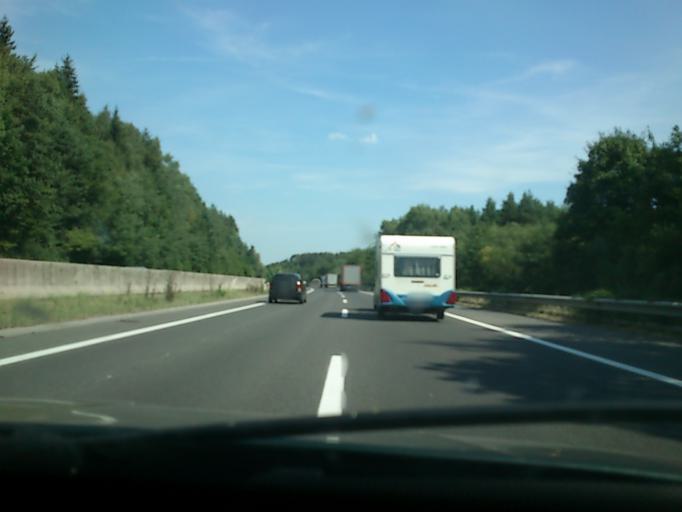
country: AT
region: Lower Austria
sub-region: Politischer Bezirk Neunkirchen
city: Seebenstein
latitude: 47.6925
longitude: 16.1295
